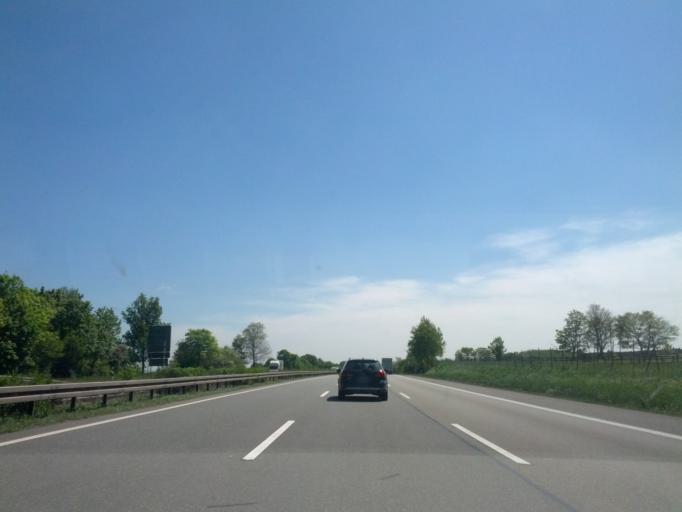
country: DE
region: Thuringia
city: Emleben
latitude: 50.9074
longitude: 10.6629
